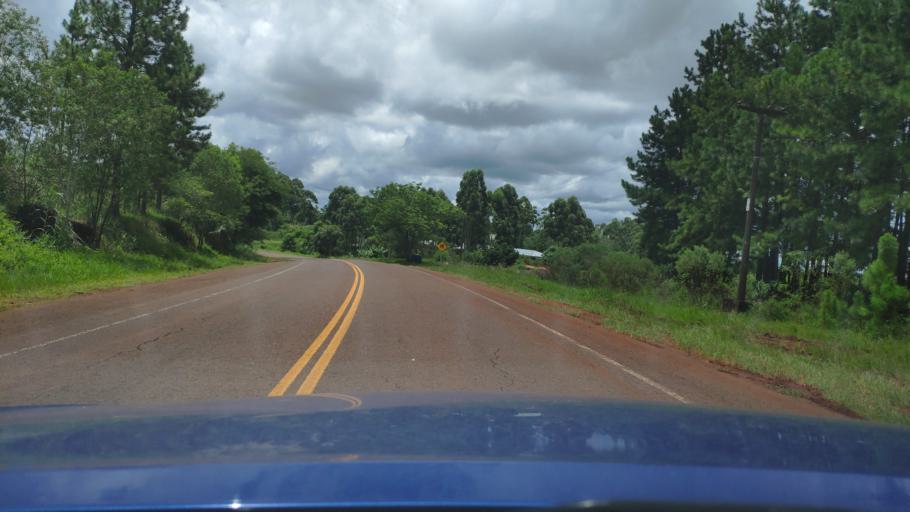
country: AR
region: Misiones
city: Dos Arroyos
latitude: -27.7281
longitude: -55.2672
